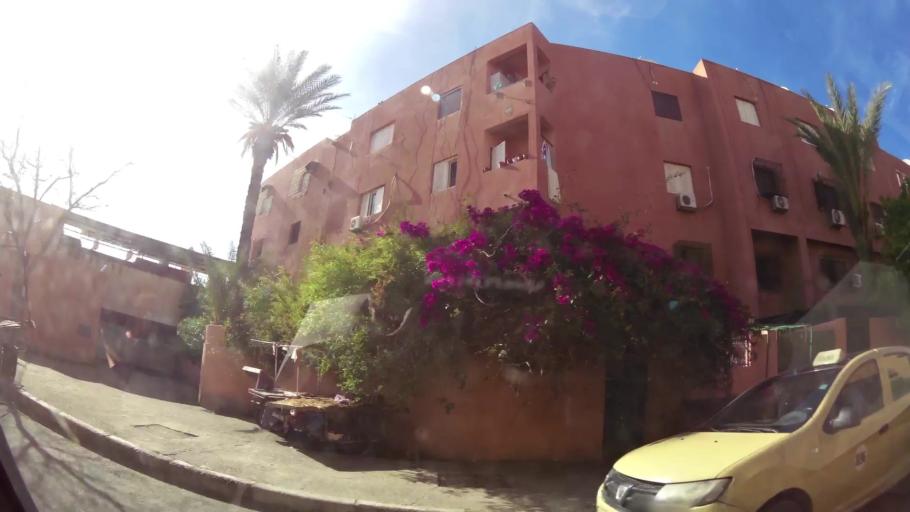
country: MA
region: Marrakech-Tensift-Al Haouz
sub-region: Marrakech
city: Marrakesh
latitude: 31.6602
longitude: -8.0110
